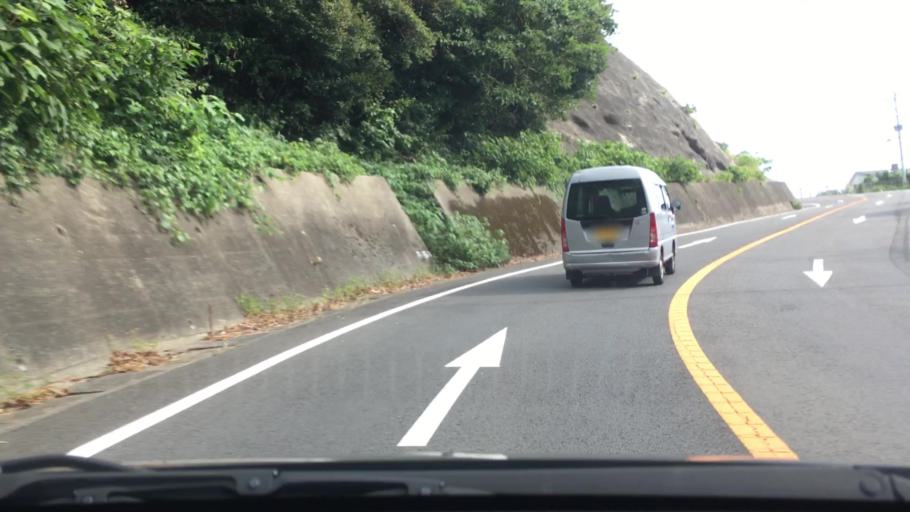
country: JP
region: Nagasaki
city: Togitsu
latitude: 32.8375
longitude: 129.7052
